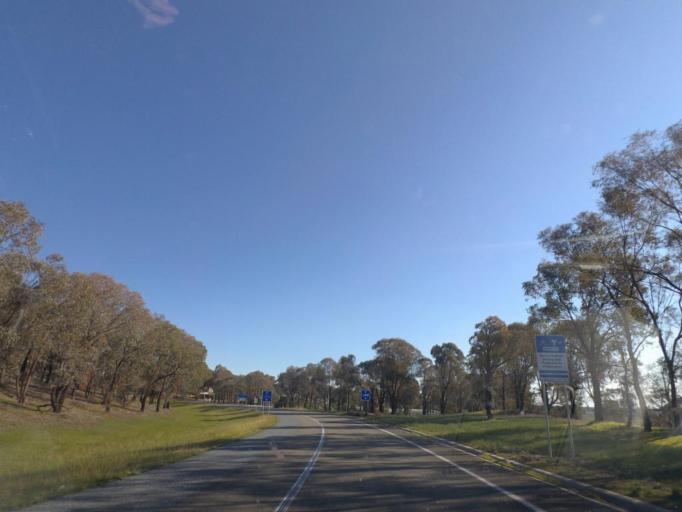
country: AU
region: Victoria
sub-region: Benalla
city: Benalla
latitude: -36.5001
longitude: 146.1048
